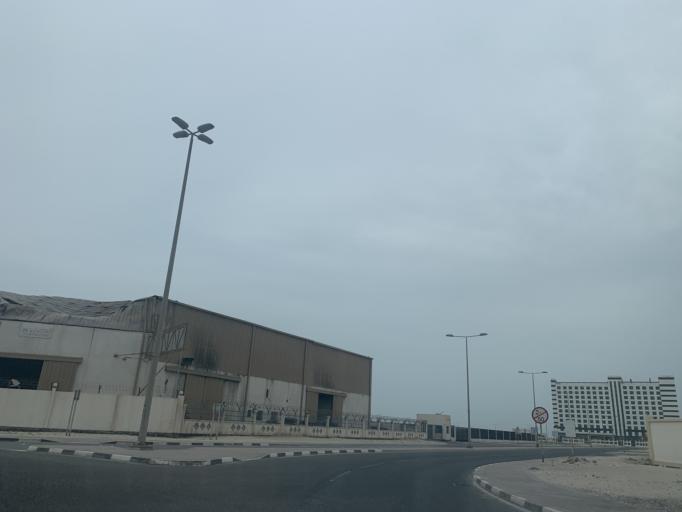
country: BH
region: Muharraq
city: Al Hadd
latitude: 26.2103
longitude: 50.6795
